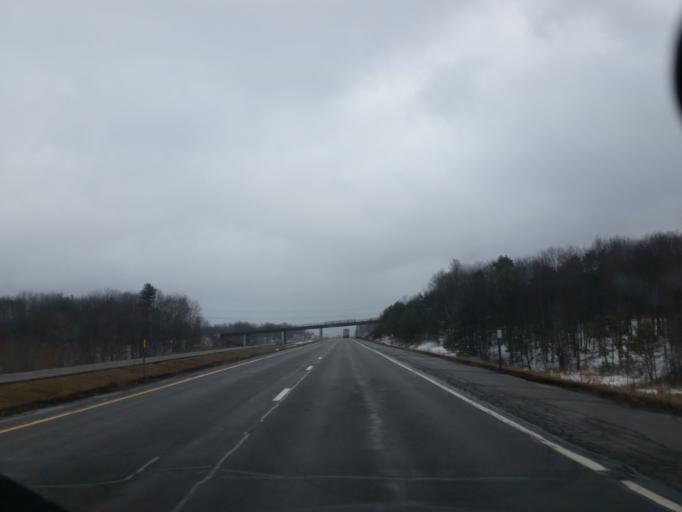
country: US
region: New York
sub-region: Chenango County
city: Lakeview
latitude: 42.3223
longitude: -75.9749
